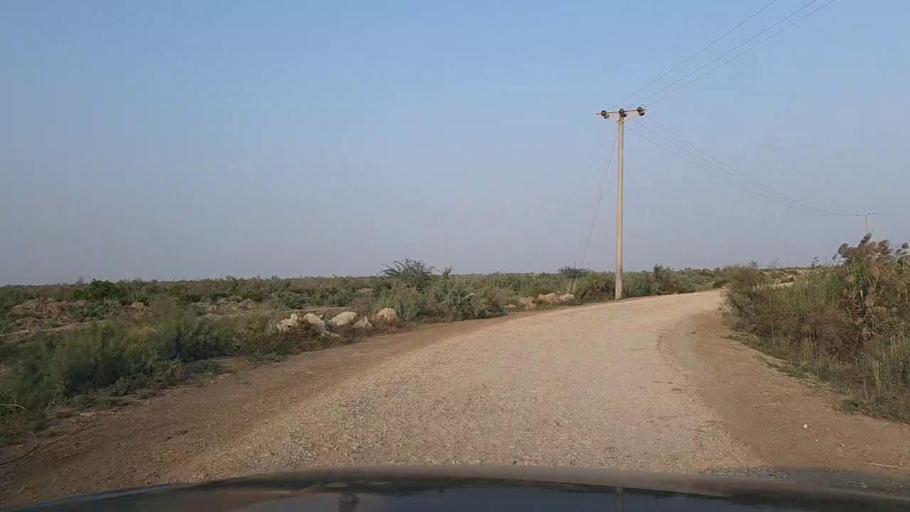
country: PK
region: Sindh
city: Mirpur Sakro
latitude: 24.4167
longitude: 67.7332
